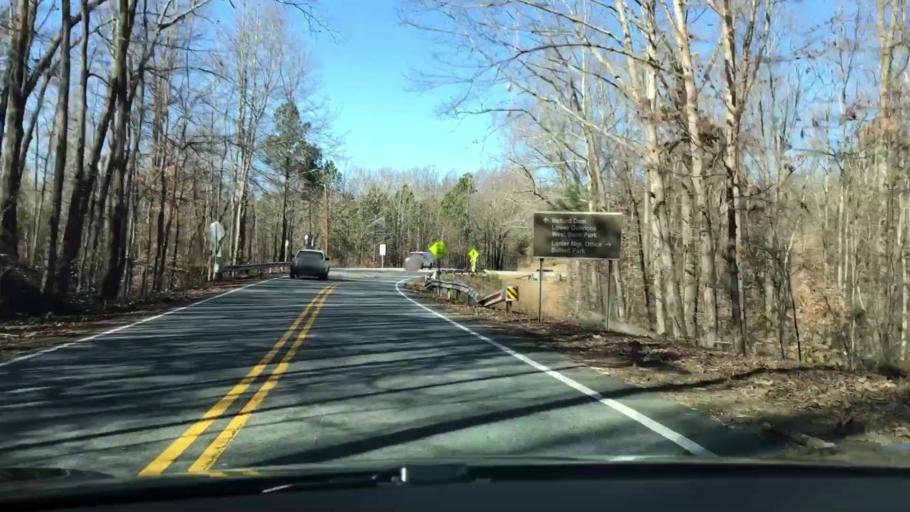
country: US
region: Georgia
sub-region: Gwinnett County
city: Sugar Hill
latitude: 34.1538
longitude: -84.0703
